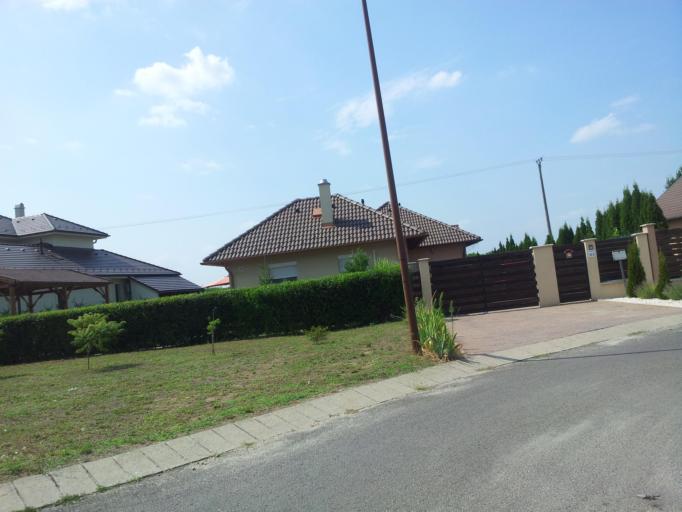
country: HU
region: Pest
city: Orbottyan
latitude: 47.6621
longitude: 19.2529
